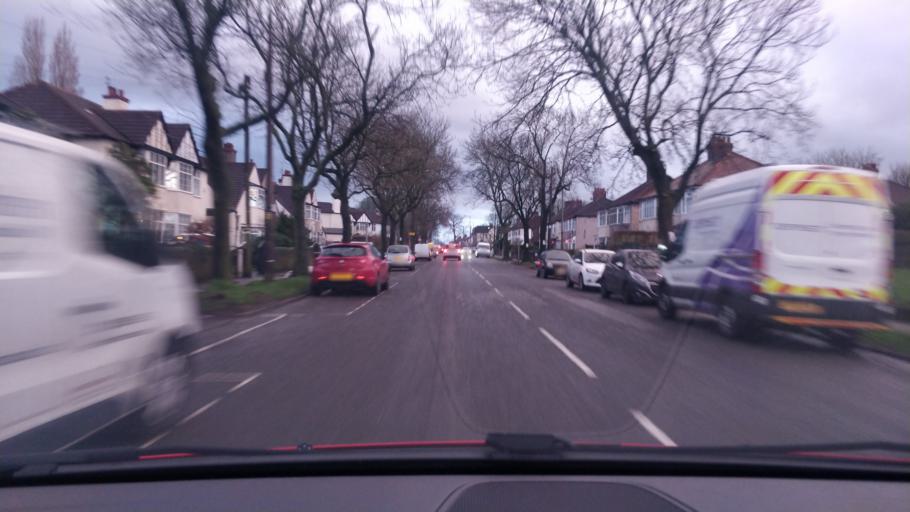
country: GB
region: England
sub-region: Knowsley
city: Huyton
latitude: 53.4131
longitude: -2.8923
